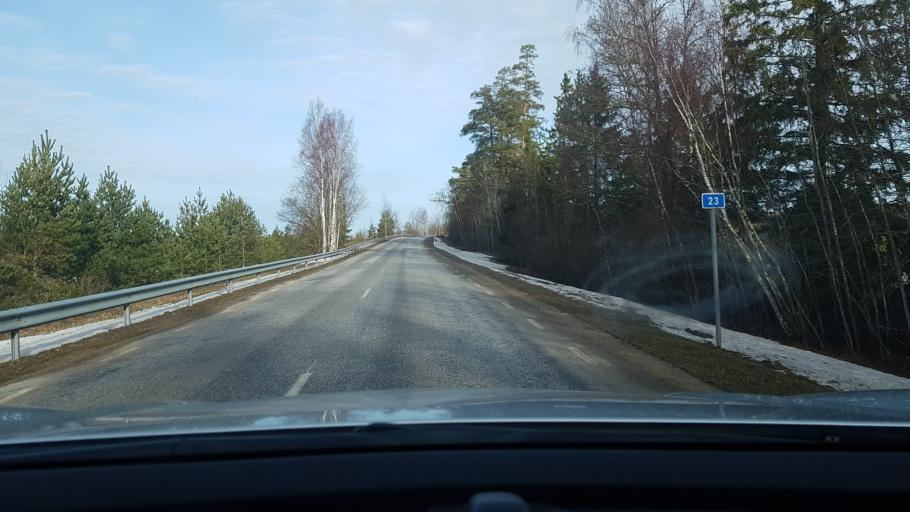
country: EE
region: Saare
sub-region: Kuressaare linn
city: Kuressaare
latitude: 58.4510
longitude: 22.7078
